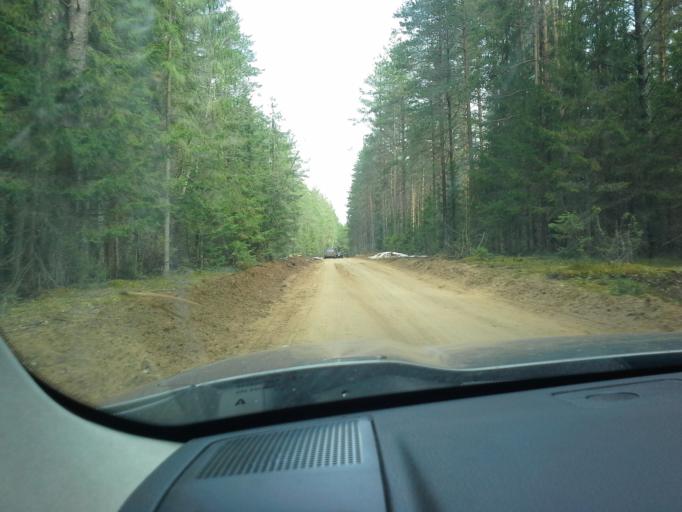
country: RU
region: Tverskaya
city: Ostashkov
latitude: 57.3442
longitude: 33.1090
